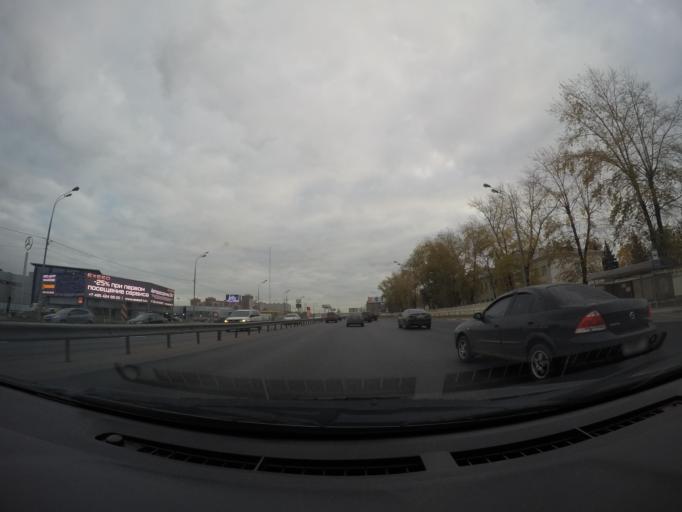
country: RU
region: Moskovskaya
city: Reutov
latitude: 55.7832
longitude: 37.8701
